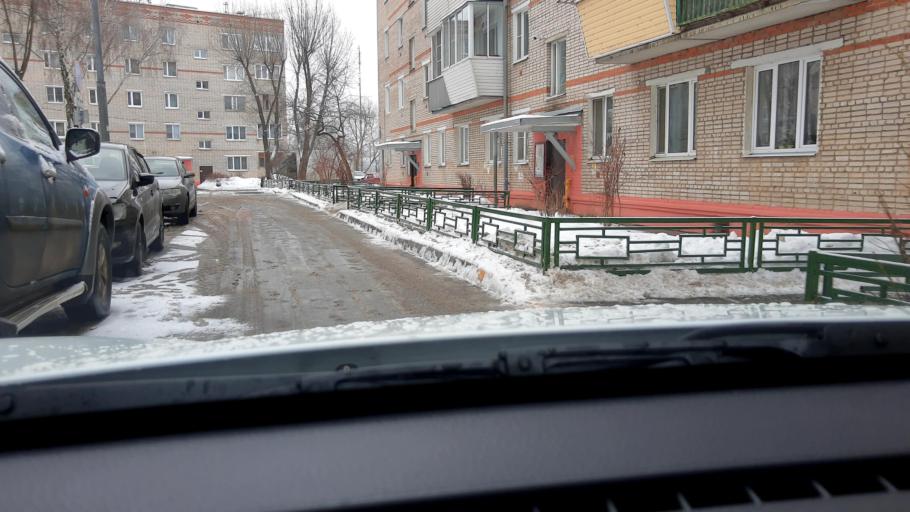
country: RU
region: Moskovskaya
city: Dubrovitsy
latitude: 55.4857
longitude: 37.4952
